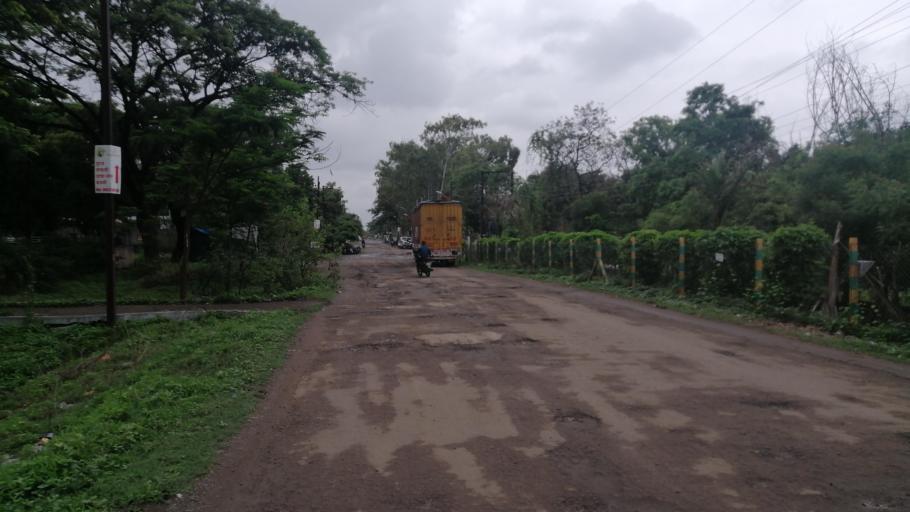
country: IN
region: Maharashtra
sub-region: Aurangabad Division
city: Aurangabad
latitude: 19.8761
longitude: 75.3780
